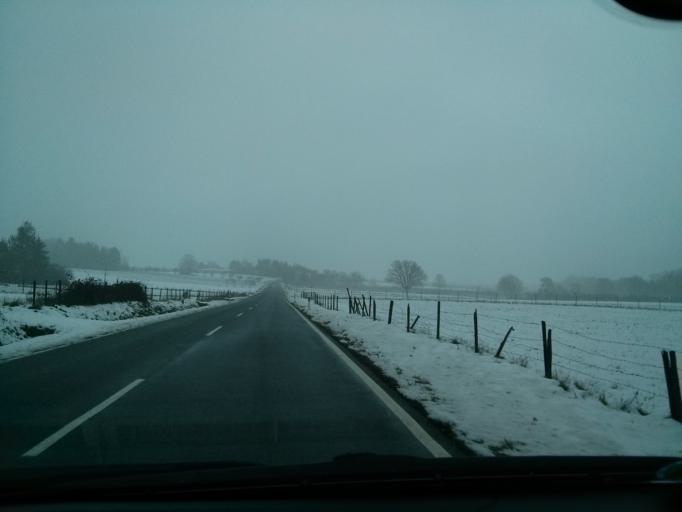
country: DE
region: Rheinland-Pfalz
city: Kalenborn
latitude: 50.5778
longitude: 6.9898
